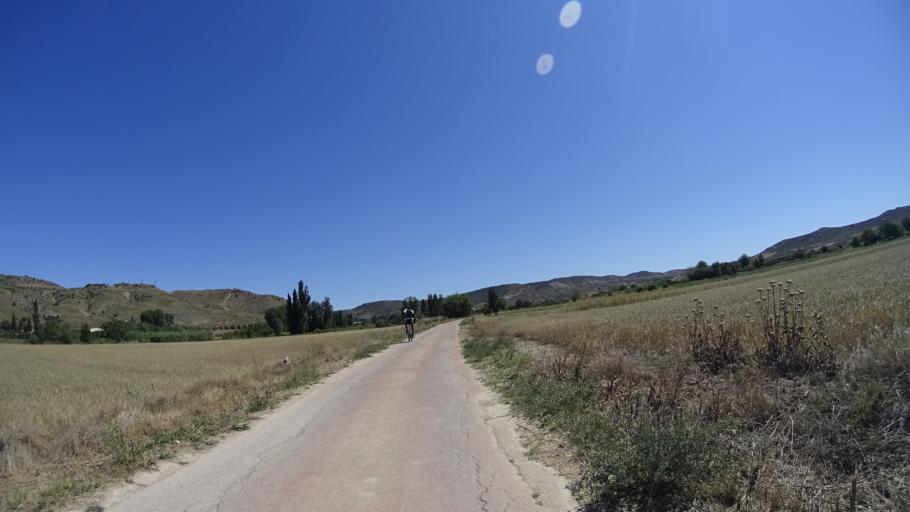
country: ES
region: Madrid
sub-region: Provincia de Madrid
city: Carabana
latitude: 40.2430
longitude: -3.2483
